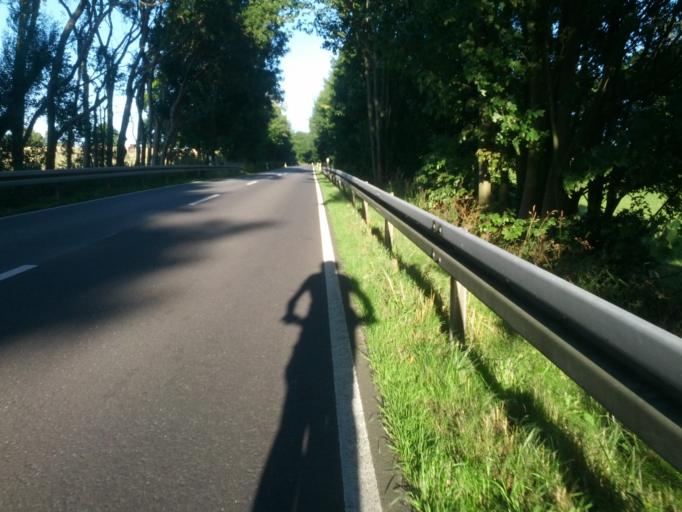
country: DE
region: Mecklenburg-Vorpommern
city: Bastorf
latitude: 54.1076
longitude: 11.6656
